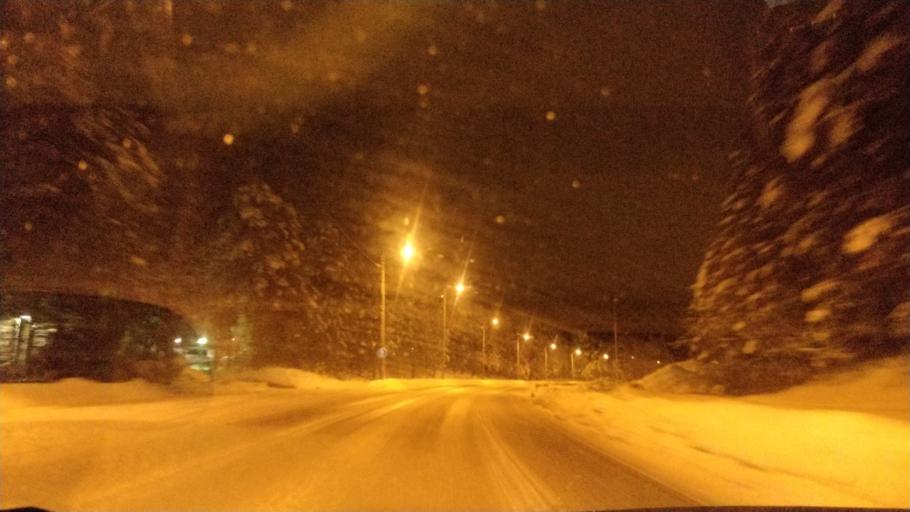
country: FI
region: Lapland
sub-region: Rovaniemi
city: Rovaniemi
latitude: 66.3766
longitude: 25.3830
